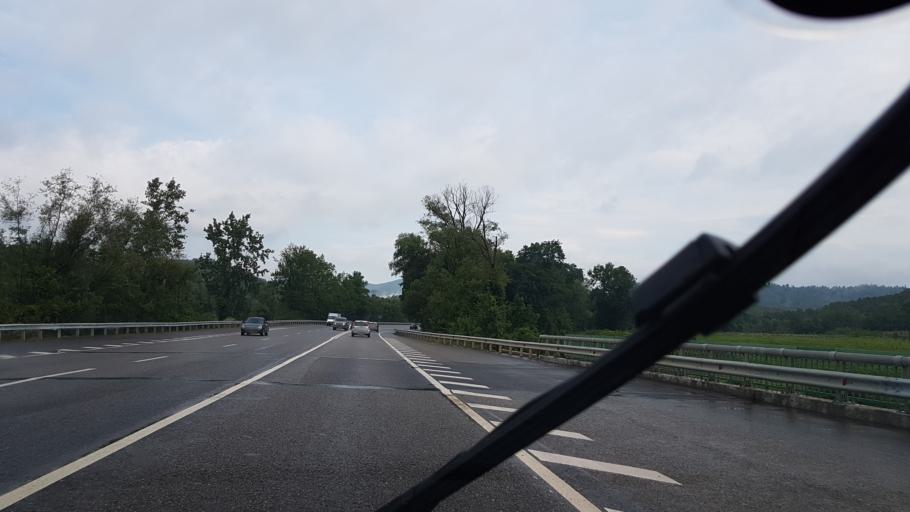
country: RU
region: Krasnodarskiy
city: Dzhubga
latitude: 44.4016
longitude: 38.7375
